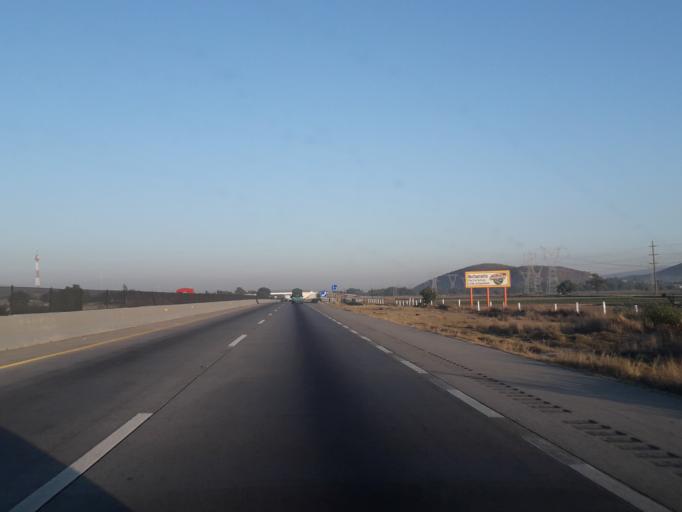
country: MX
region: Puebla
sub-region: Tepeaca
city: San Mateo Parra
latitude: 18.9919
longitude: -97.8562
